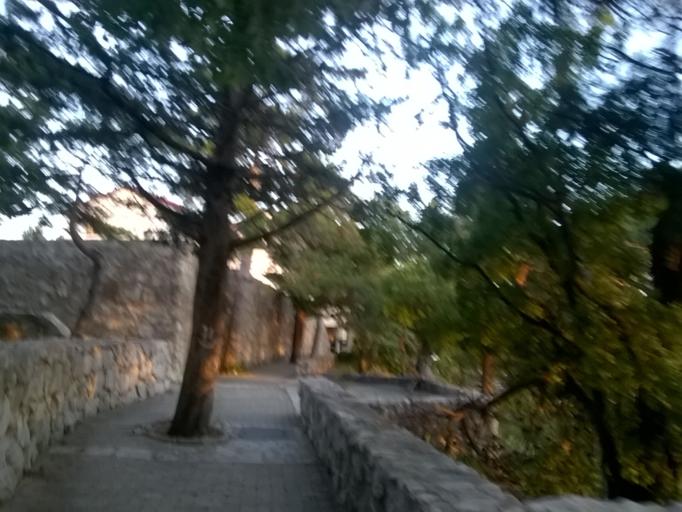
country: HR
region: Licko-Senjska
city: Karlobag
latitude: 44.5290
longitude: 15.0688
